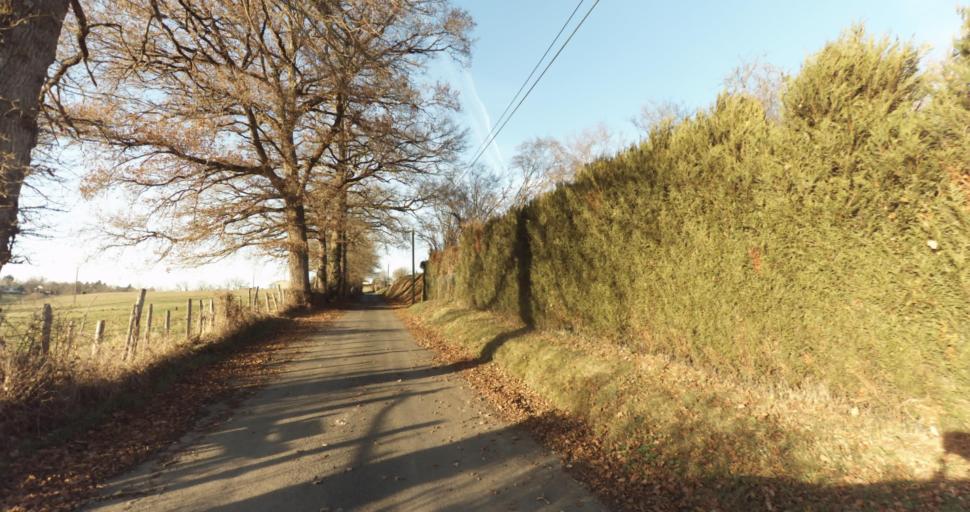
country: FR
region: Limousin
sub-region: Departement de la Haute-Vienne
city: Aixe-sur-Vienne
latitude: 45.7823
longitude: 1.1507
